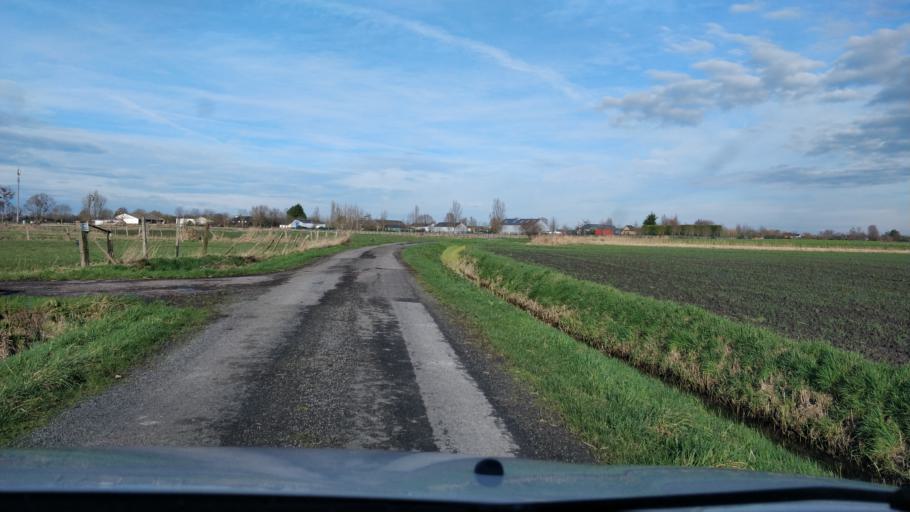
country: FR
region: Brittany
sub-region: Departement d'Ille-et-Vilaine
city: La Fresnais
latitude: 48.5791
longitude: -1.8302
